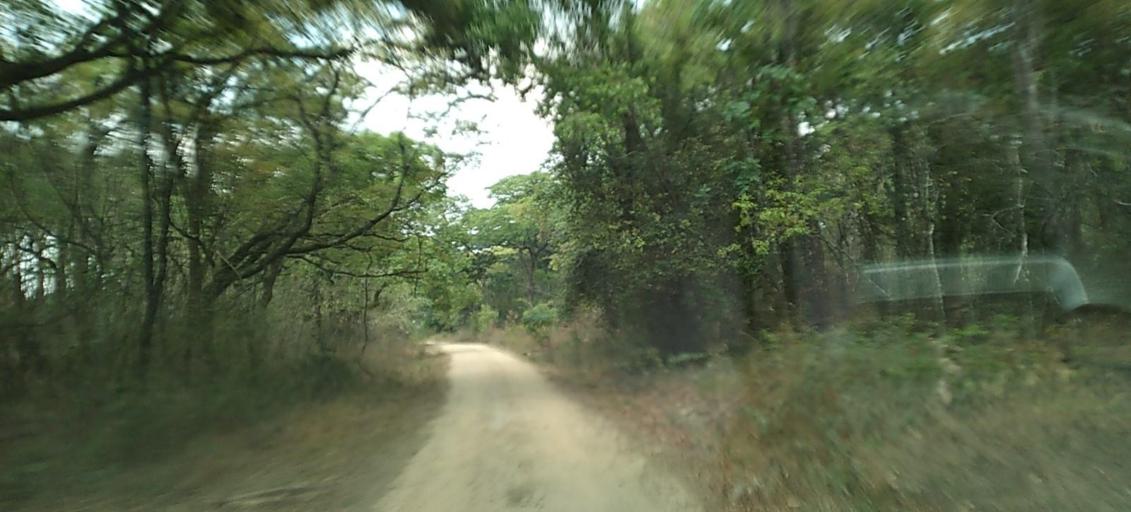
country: ZM
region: Copperbelt
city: Chingola
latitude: -12.7541
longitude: 27.7167
